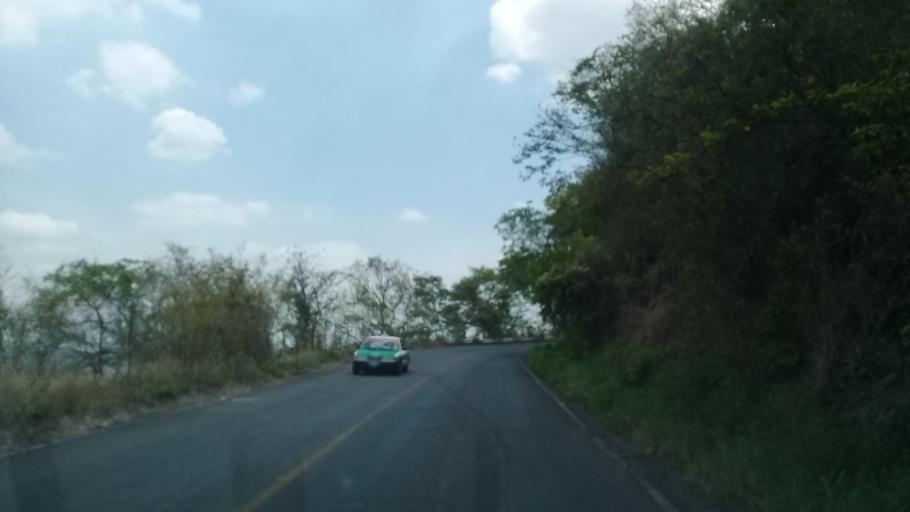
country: MX
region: Veracruz
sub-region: Emiliano Zapata
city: Plan del Rio
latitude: 19.4154
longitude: -96.6124
